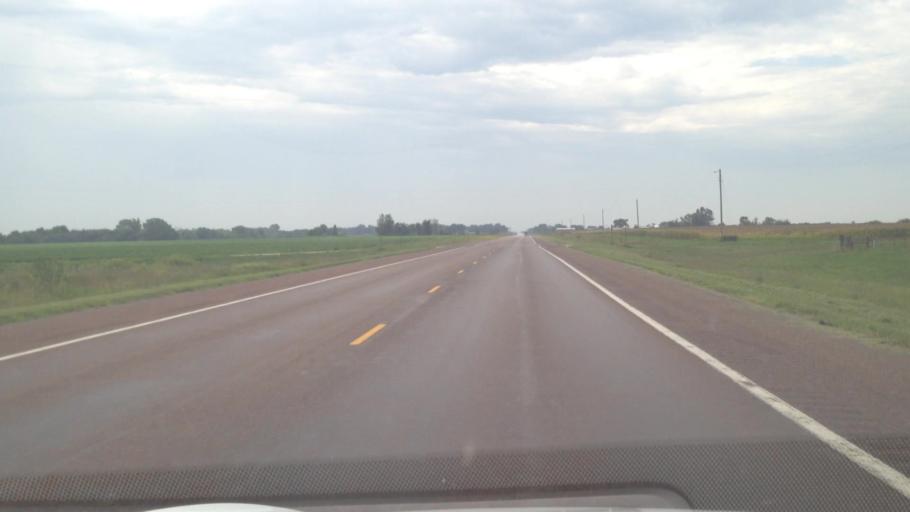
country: US
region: Kansas
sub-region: Crawford County
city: Girard
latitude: 37.4562
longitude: -94.8330
